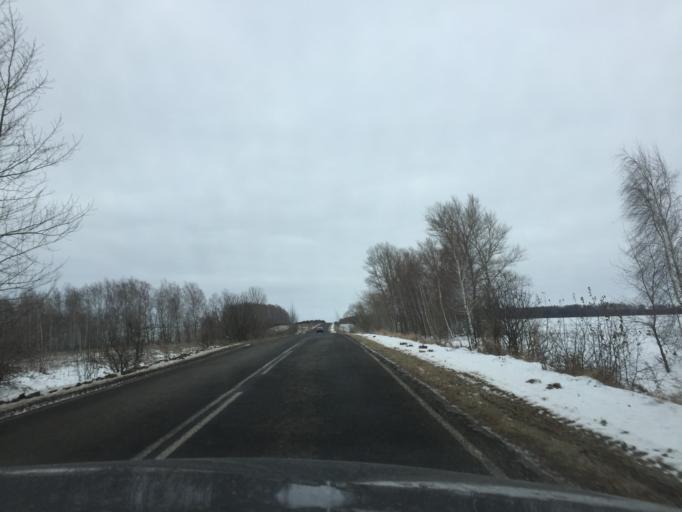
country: RU
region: Tula
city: Shchekino
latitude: 53.8165
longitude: 37.5327
